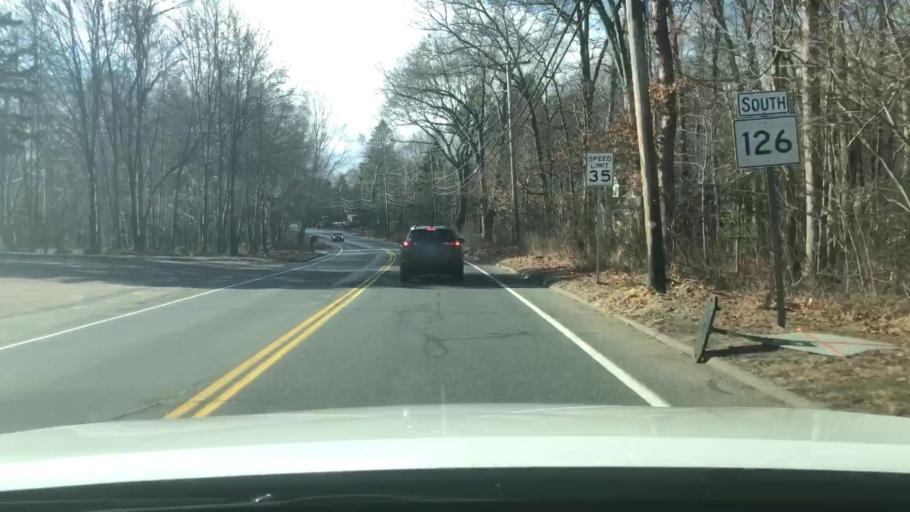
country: US
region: Rhode Island
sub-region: Providence County
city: Woonsocket
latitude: 42.0397
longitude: -71.4903
